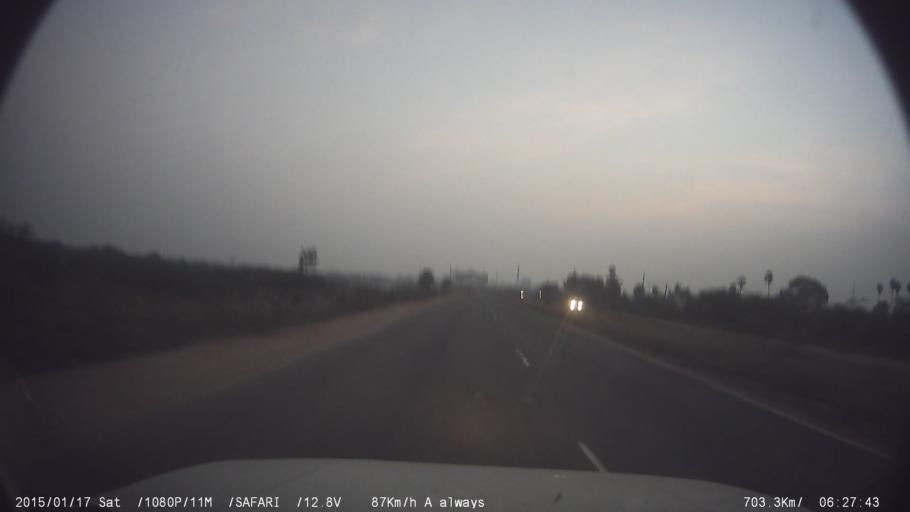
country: IN
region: Tamil Nadu
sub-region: Kancheepuram
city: Sriperumbudur
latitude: 12.9325
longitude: 79.9000
